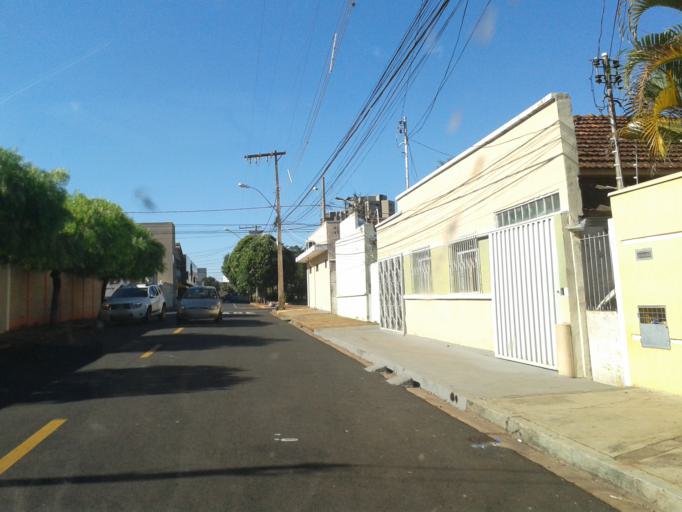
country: BR
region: Minas Gerais
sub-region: Uberaba
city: Uberaba
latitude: -19.7508
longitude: -47.9503
